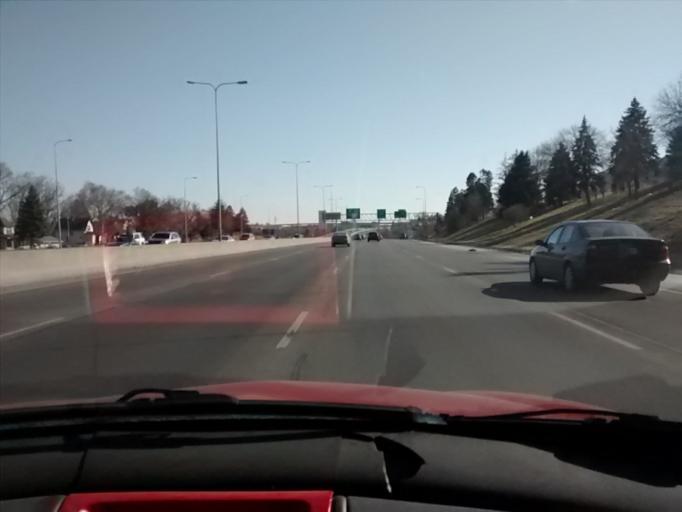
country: US
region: Nebraska
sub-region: Douglas County
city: Omaha
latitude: 41.2440
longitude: -95.9538
